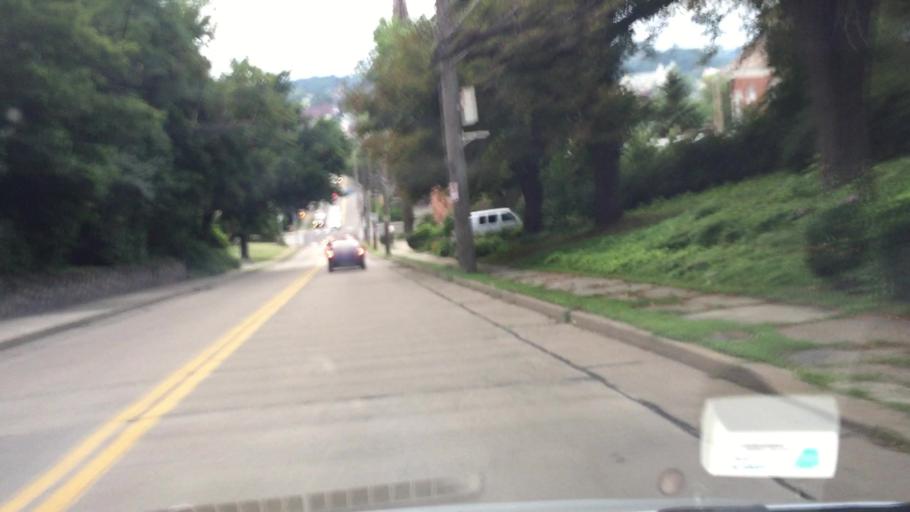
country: US
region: Pennsylvania
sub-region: Allegheny County
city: Bloomfield
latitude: 40.4486
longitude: -79.9288
